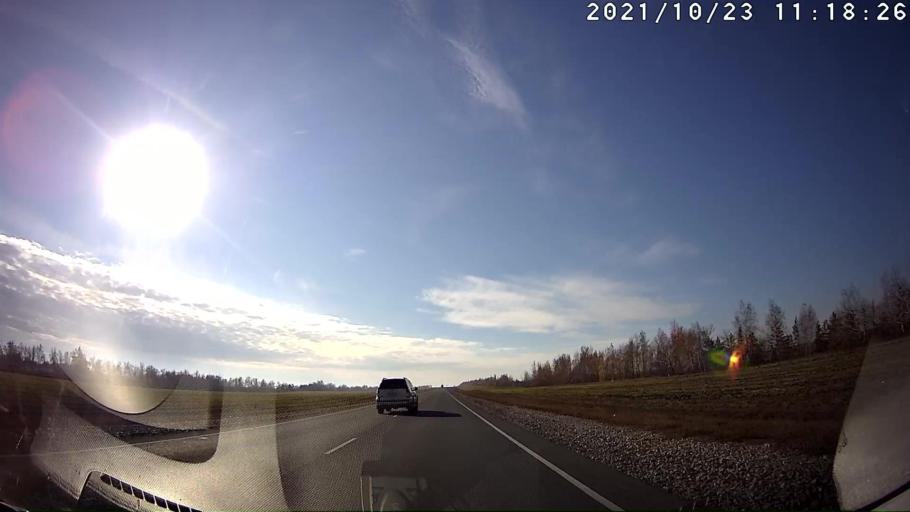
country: RU
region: Saratov
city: Kamenskiy
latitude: 50.8966
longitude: 45.5932
